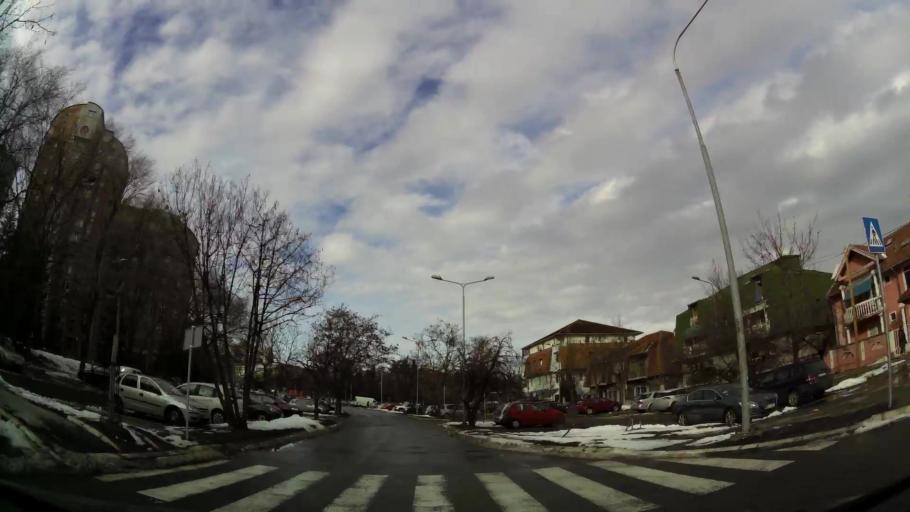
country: RS
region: Central Serbia
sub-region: Belgrade
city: Rakovica
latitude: 44.7402
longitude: 20.4260
